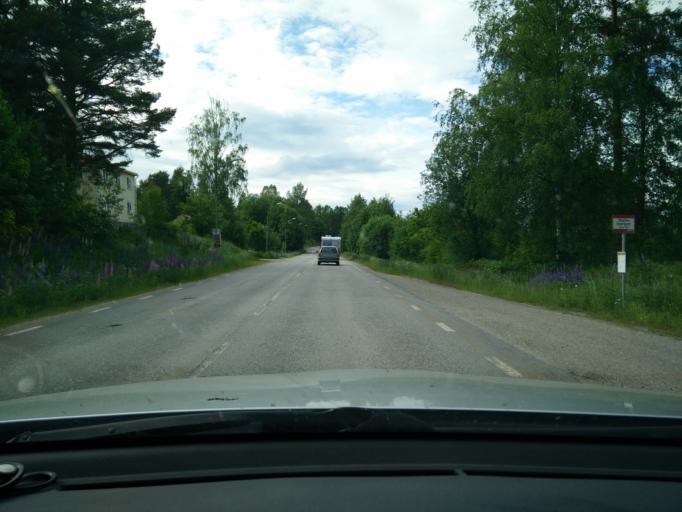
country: SE
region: Gaevleborg
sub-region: Nordanstigs Kommun
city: Bergsjoe
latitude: 61.9708
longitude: 17.0562
